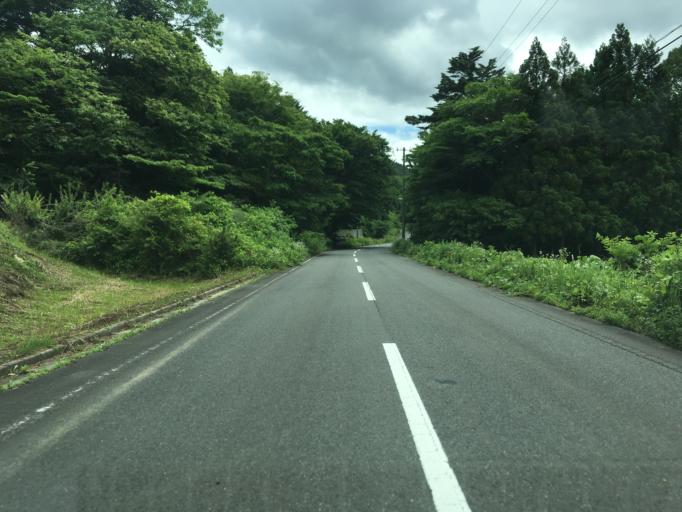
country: JP
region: Miyagi
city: Marumori
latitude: 37.7181
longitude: 140.8855
